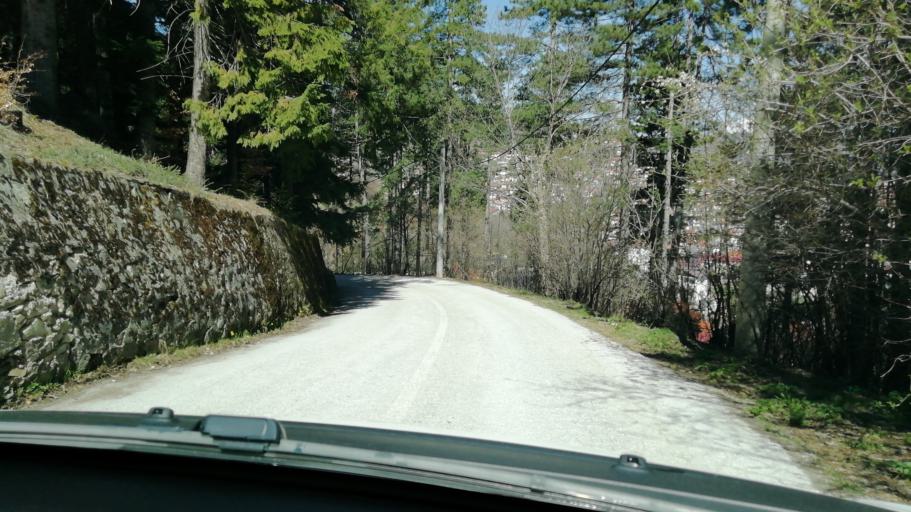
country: MK
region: Krusevo
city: Krushevo
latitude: 41.3639
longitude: 21.2516
